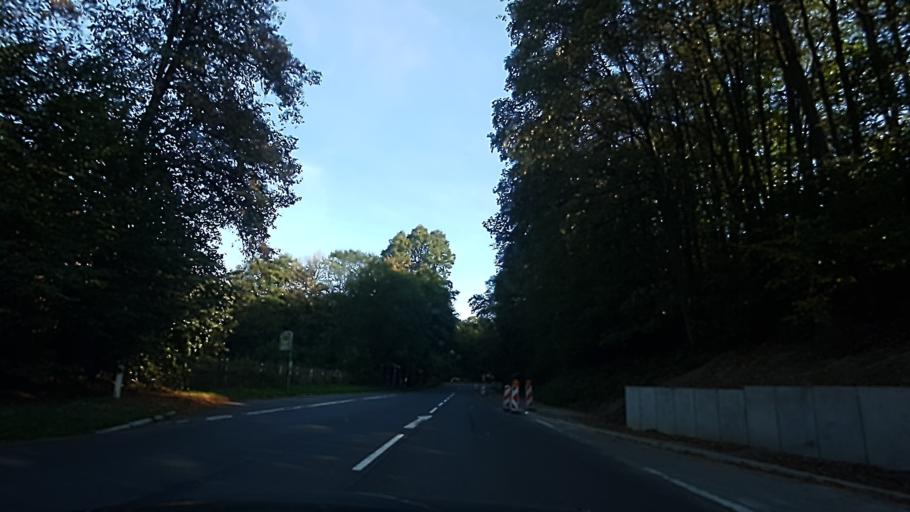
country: DE
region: North Rhine-Westphalia
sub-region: Regierungsbezirk Koln
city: Marienheide
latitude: 51.0959
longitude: 7.5230
